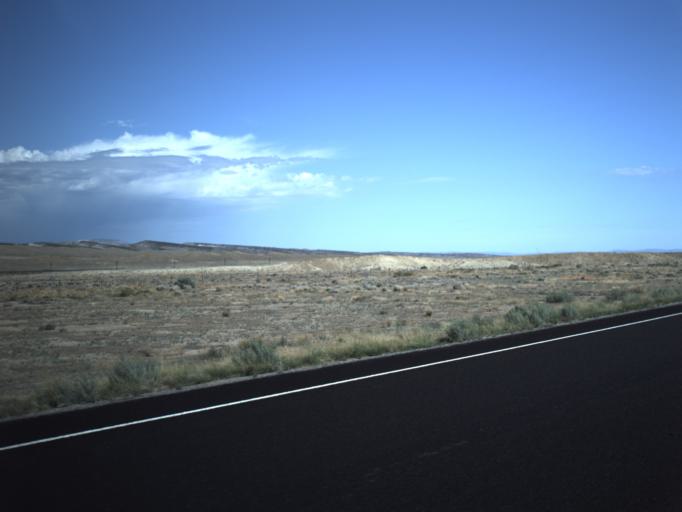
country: US
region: Utah
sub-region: Carbon County
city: East Carbon City
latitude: 39.1794
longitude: -110.3383
